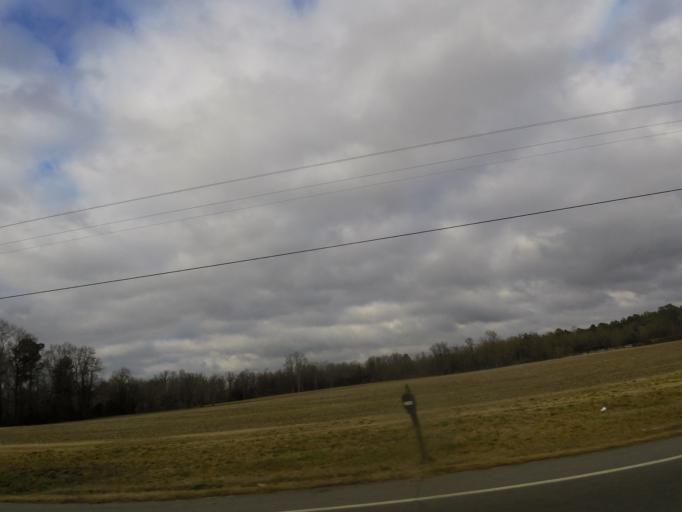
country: US
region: North Carolina
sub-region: Edgecombe County
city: Pinetops
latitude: 35.8114
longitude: -77.6531
